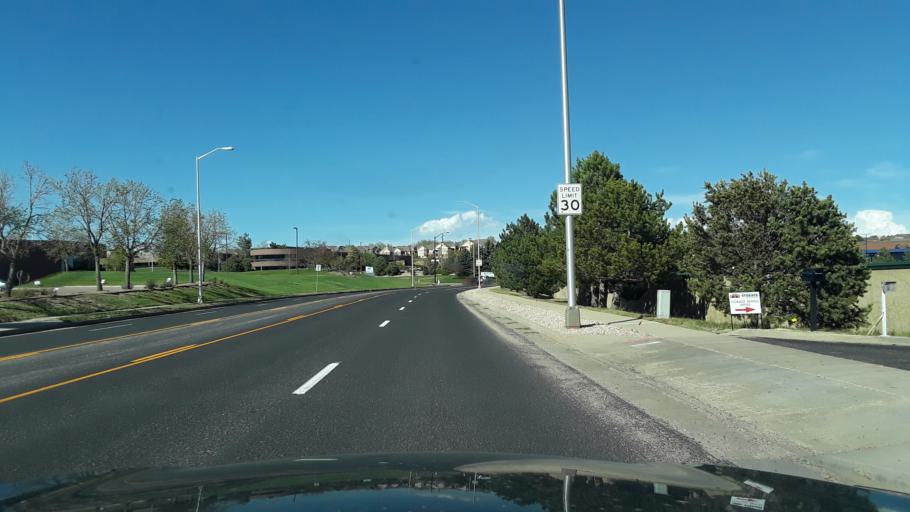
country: US
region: Colorado
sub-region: El Paso County
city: Air Force Academy
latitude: 38.9517
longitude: -104.7933
